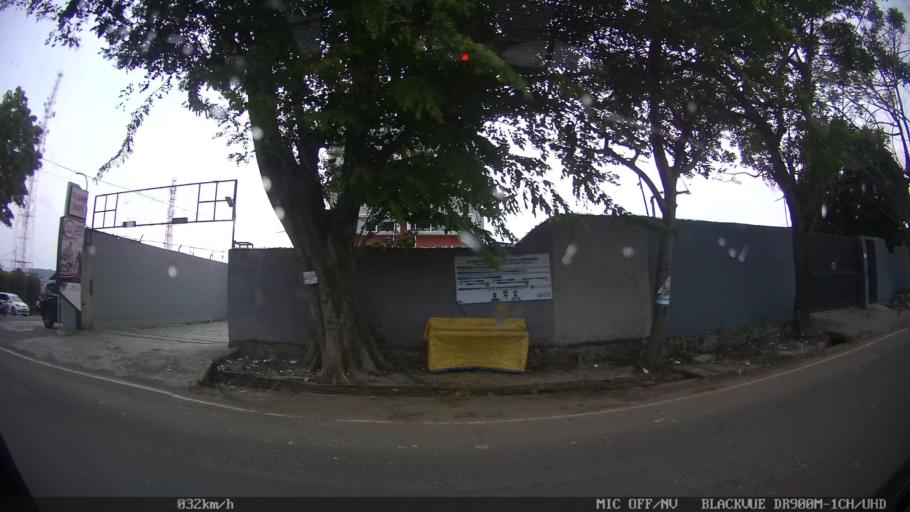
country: ID
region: Lampung
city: Kedaton
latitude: -5.3959
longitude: 105.2812
